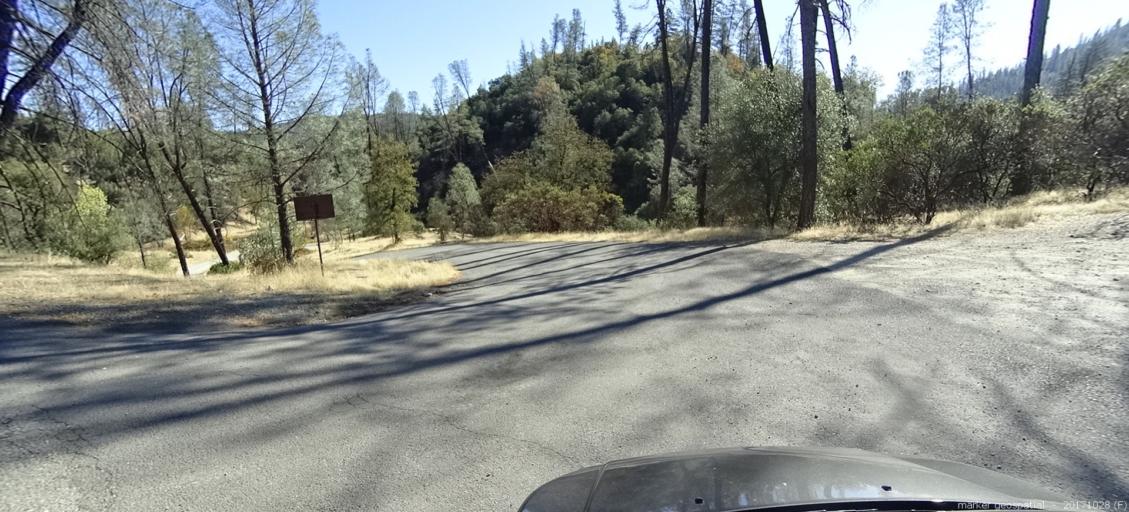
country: US
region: California
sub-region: Shasta County
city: Shasta
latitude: 40.5801
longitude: -122.5369
